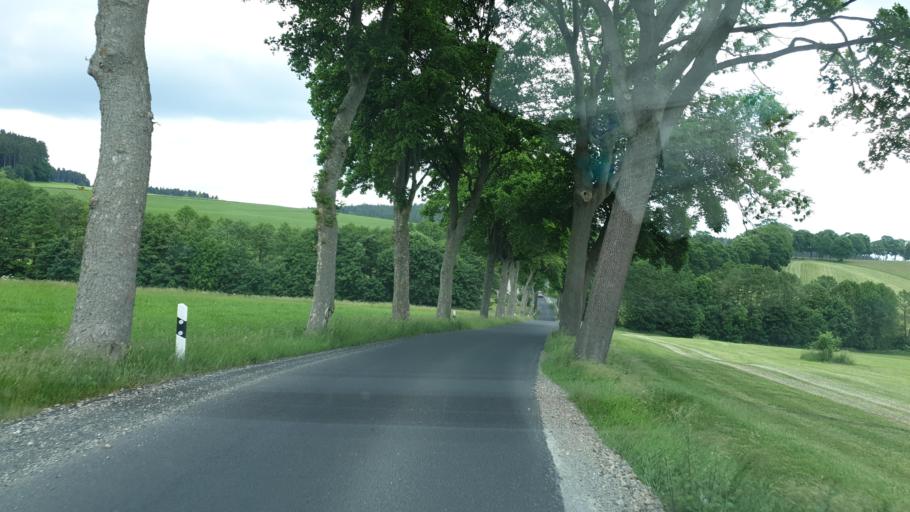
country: DE
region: Saxony
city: Lengefeld
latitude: 50.6858
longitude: 13.1796
